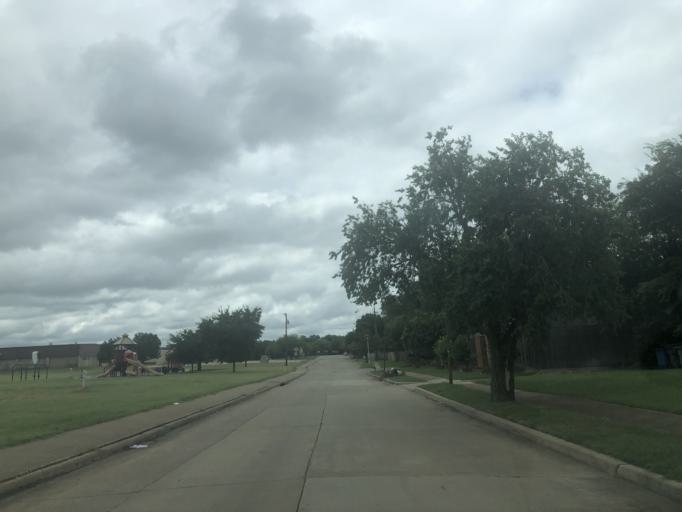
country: US
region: Texas
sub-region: Dallas County
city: Duncanville
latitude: 32.6428
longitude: -96.9481
